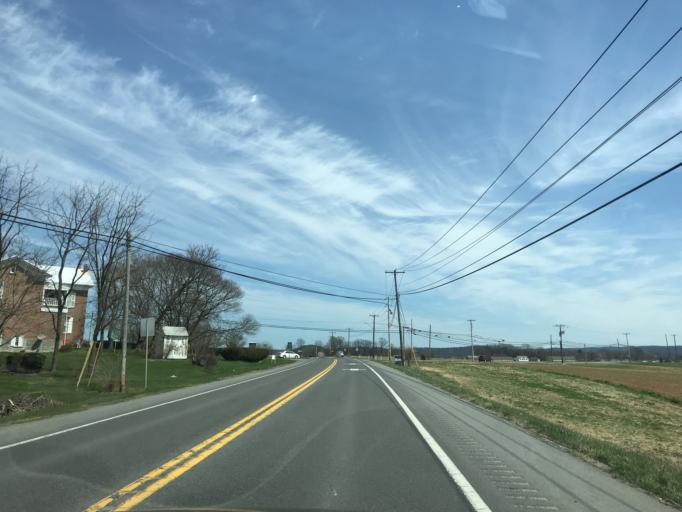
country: US
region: Pennsylvania
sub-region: Snyder County
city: Selinsgrove
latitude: 40.8051
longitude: -76.8919
